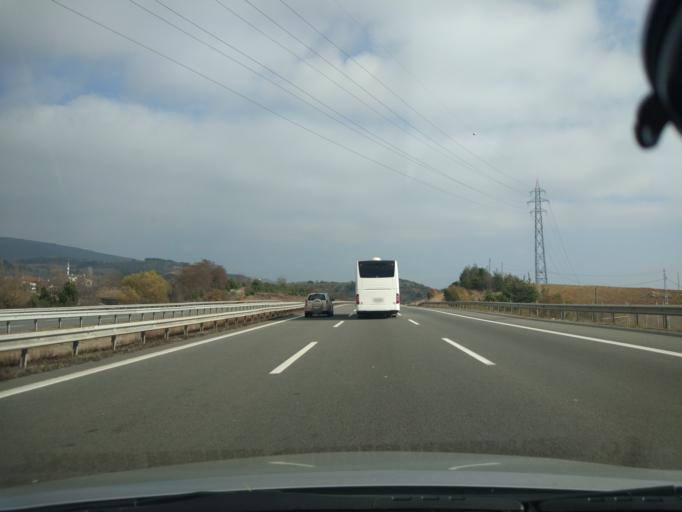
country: TR
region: Bolu
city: Bolu
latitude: 40.7691
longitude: 31.6561
